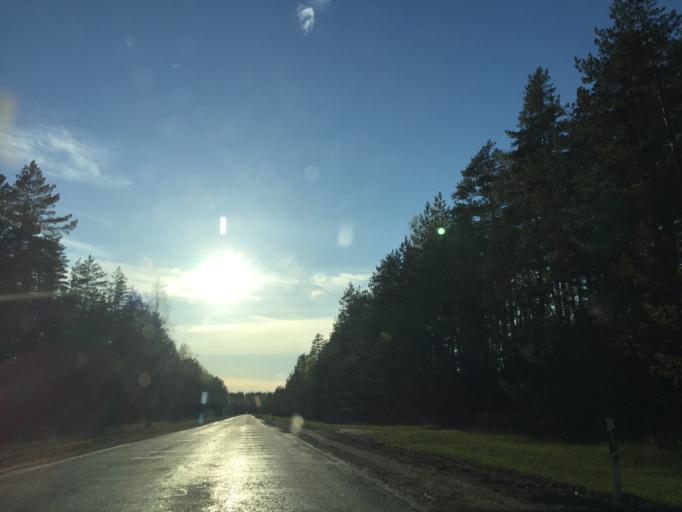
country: LV
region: Strenci
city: Seda
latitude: 57.6246
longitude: 25.7583
